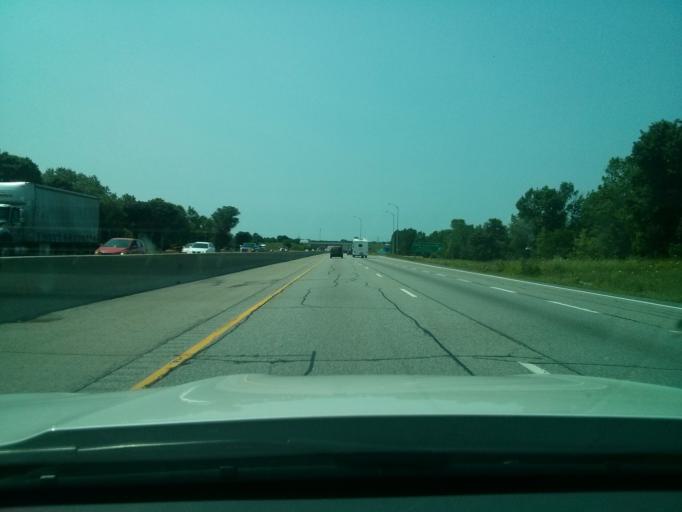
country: CA
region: Ontario
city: Brockville
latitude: 44.6148
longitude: -75.6805
